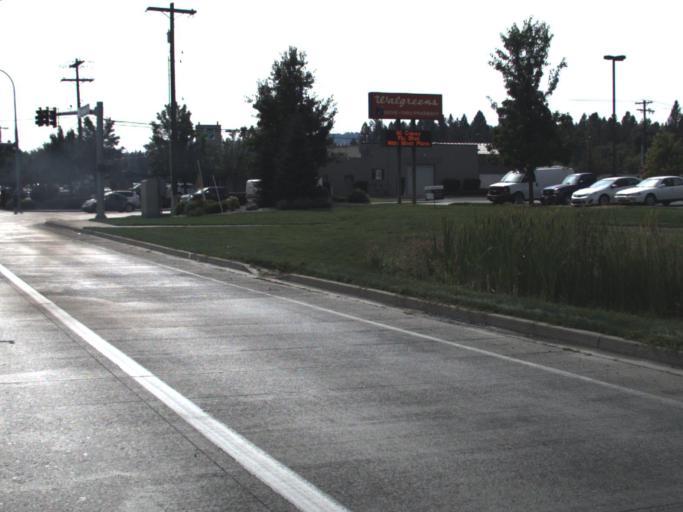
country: US
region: Washington
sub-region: Spokane County
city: Fairwood
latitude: 47.7695
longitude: -117.4044
